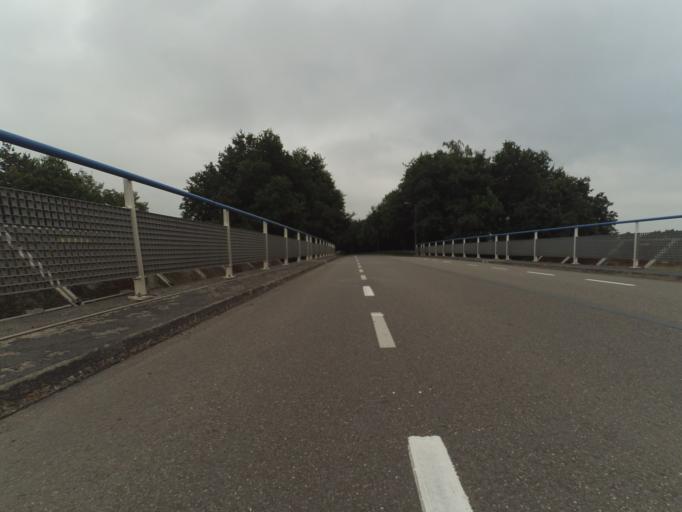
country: NL
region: Gelderland
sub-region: Gemeente Barneveld
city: Voorthuizen
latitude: 52.1728
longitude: 5.6372
